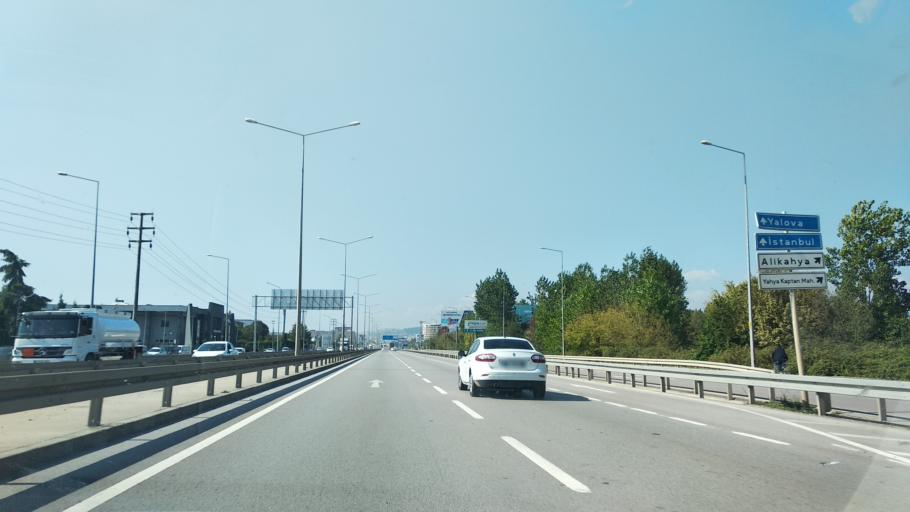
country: TR
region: Kocaeli
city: Kosekoy
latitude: 40.7569
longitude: 29.9994
